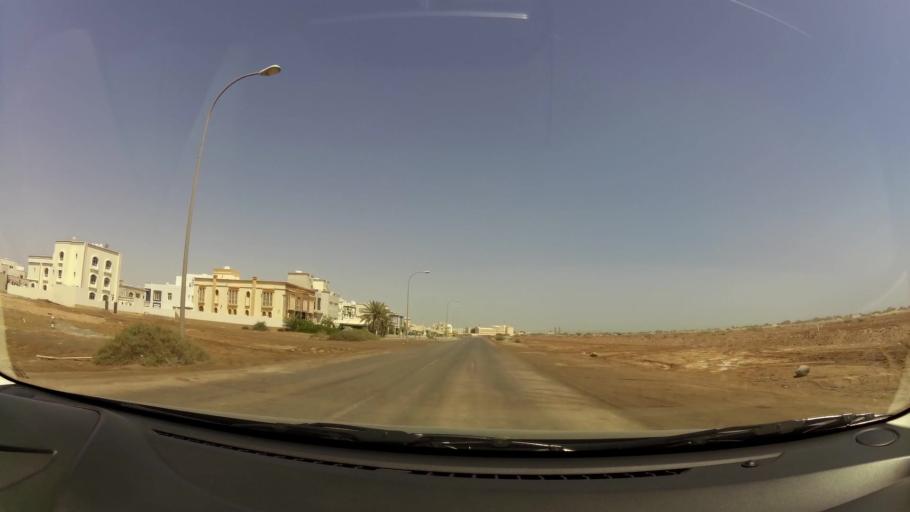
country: OM
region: Muhafazat Masqat
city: As Sib al Jadidah
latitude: 23.6257
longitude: 58.2569
